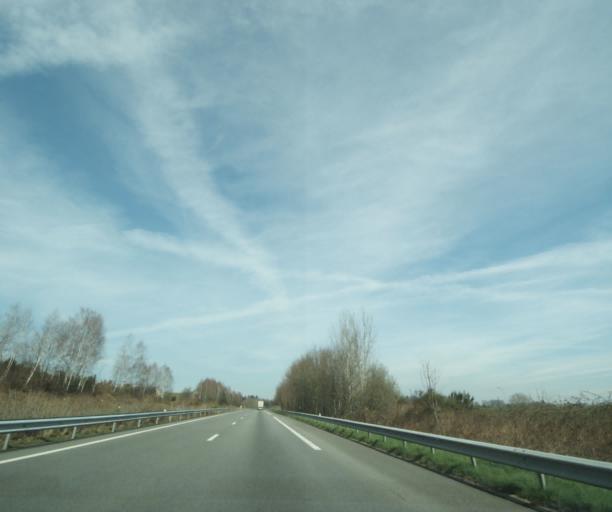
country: FR
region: Limousin
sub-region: Departement de la Correze
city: Uzerche
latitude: 45.4471
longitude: 1.5095
